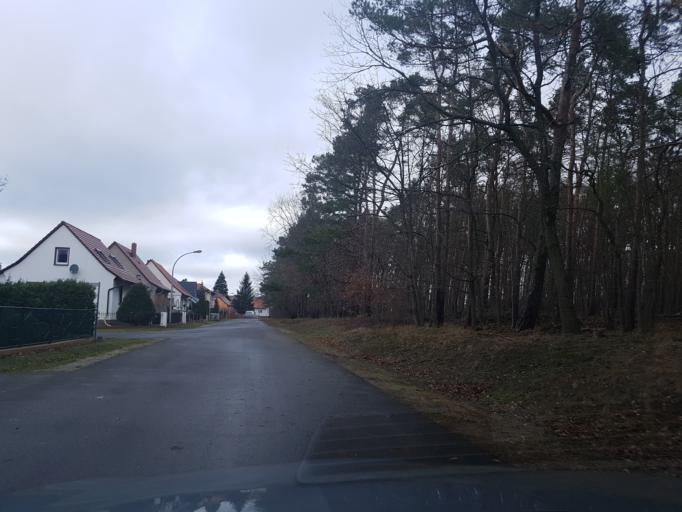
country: DE
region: Brandenburg
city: Falkenberg
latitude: 51.5858
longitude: 13.2651
